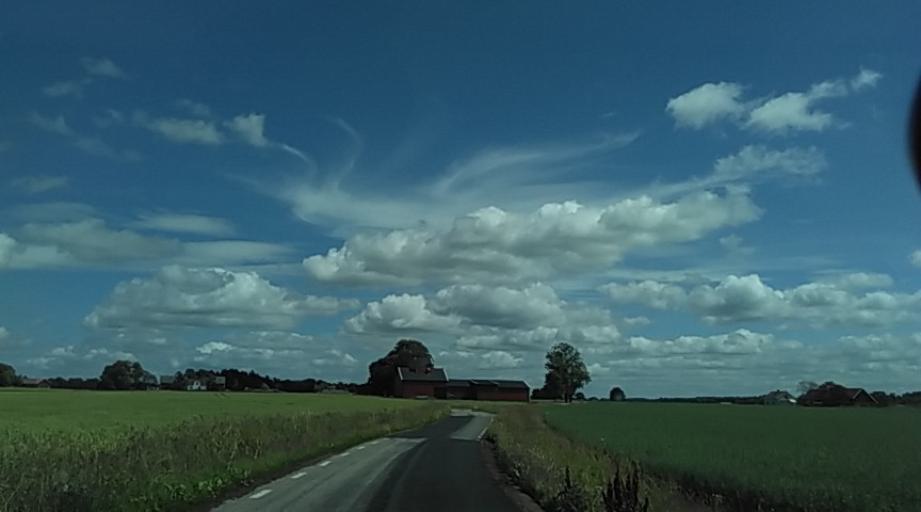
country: SE
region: Vaestra Goetaland
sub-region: Vargarda Kommun
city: Vargarda
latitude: 58.1384
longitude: 12.8485
